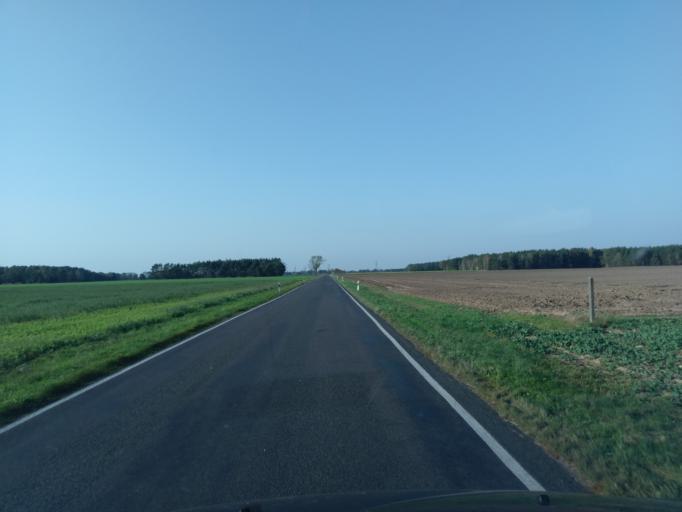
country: DE
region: Brandenburg
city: Falkenberg
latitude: 51.5488
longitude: 13.2731
